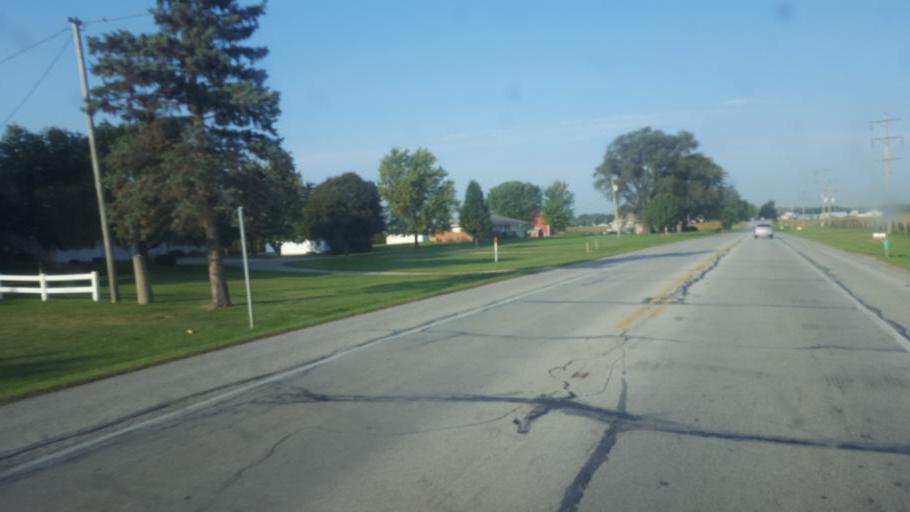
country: US
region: Indiana
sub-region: LaGrange County
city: Topeka
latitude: 41.6405
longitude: -85.5312
